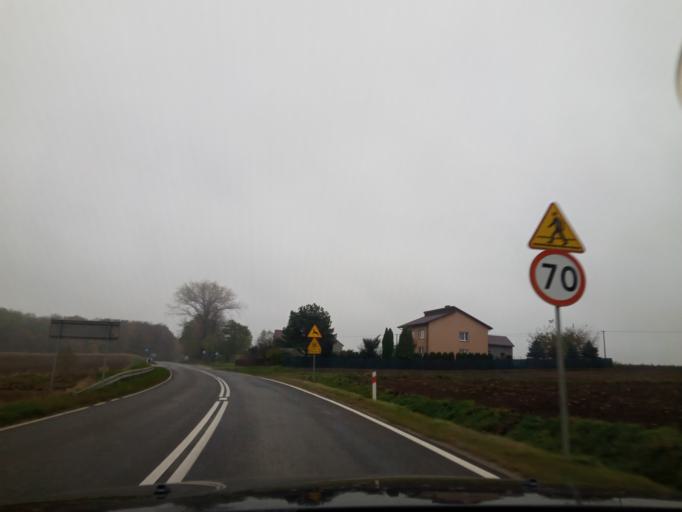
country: PL
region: Lesser Poland Voivodeship
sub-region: Powiat proszowicki
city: Klimontow
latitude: 50.2291
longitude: 20.3762
